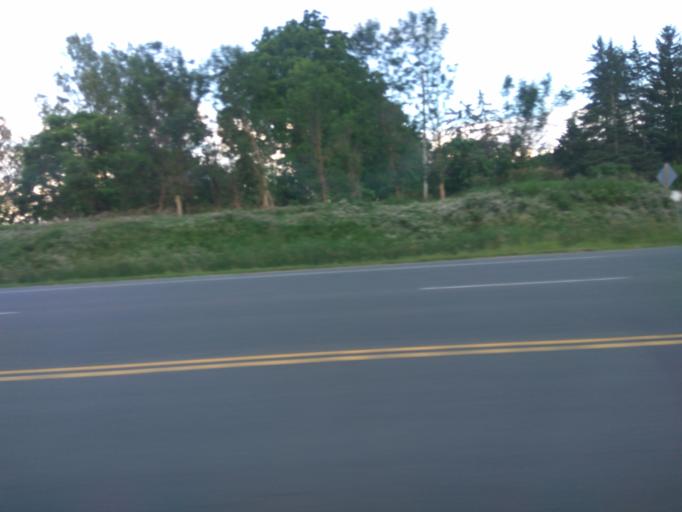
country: CA
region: Ontario
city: Stratford
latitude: 43.3700
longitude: -80.9172
